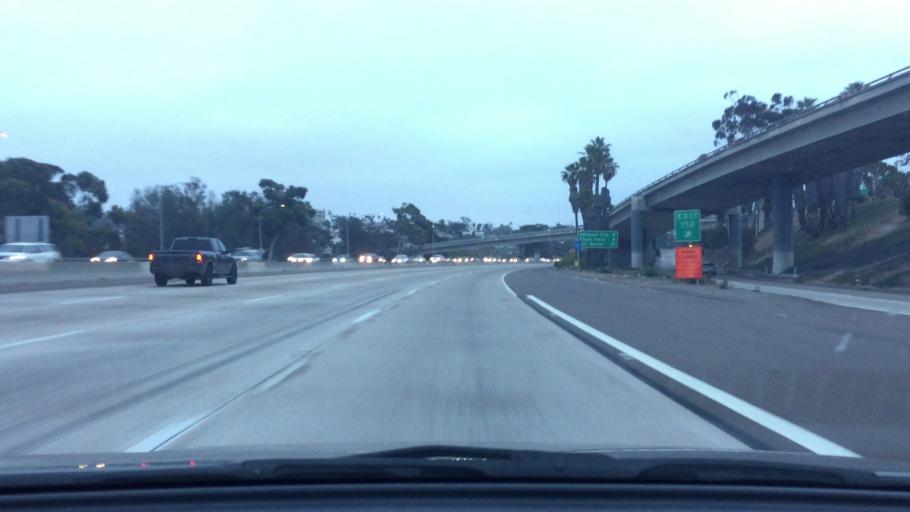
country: US
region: California
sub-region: San Diego County
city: San Diego
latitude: 32.7219
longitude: -117.1491
